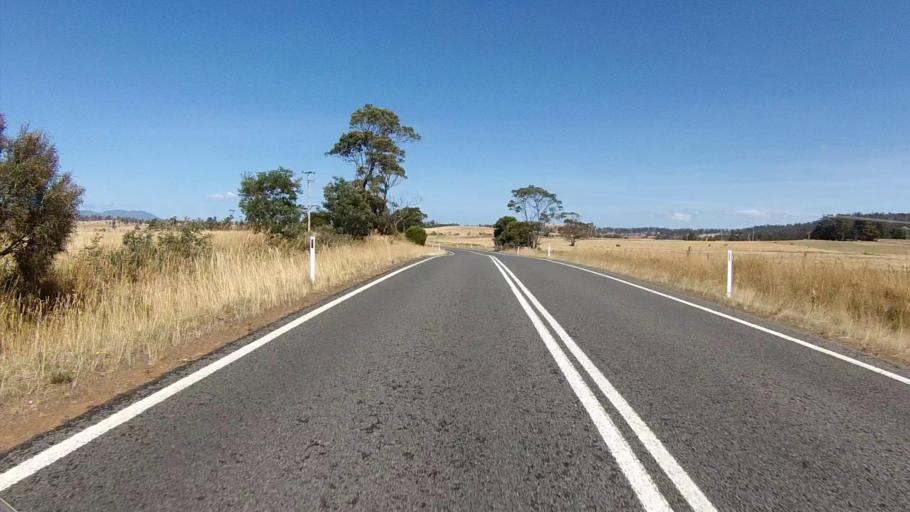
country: AU
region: Tasmania
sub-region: Sorell
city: Sorell
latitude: -42.4472
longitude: 147.9290
